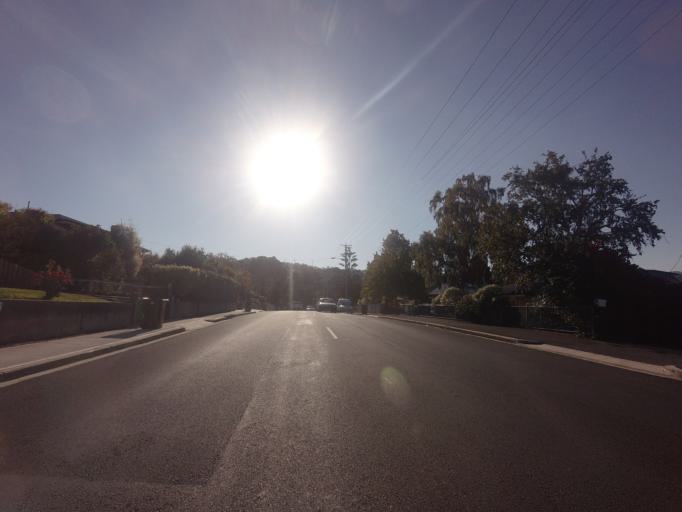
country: AU
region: Tasmania
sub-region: Glenorchy
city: West Moonah
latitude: -42.8623
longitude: 147.2870
